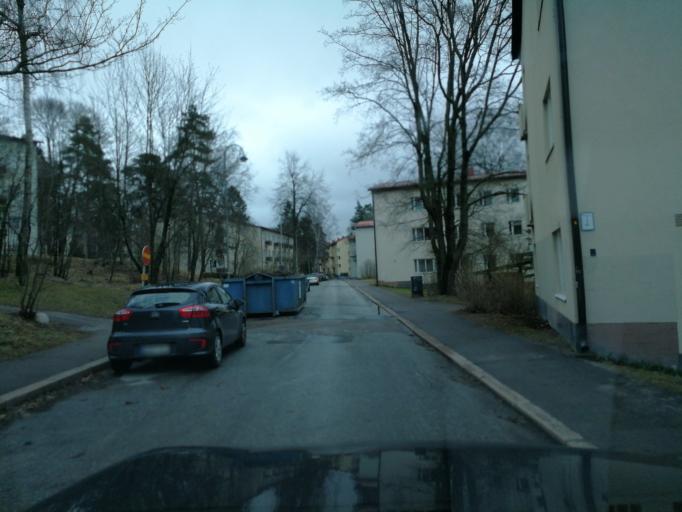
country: FI
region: Uusimaa
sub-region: Helsinki
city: Helsinki
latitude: 60.2123
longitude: 24.9535
